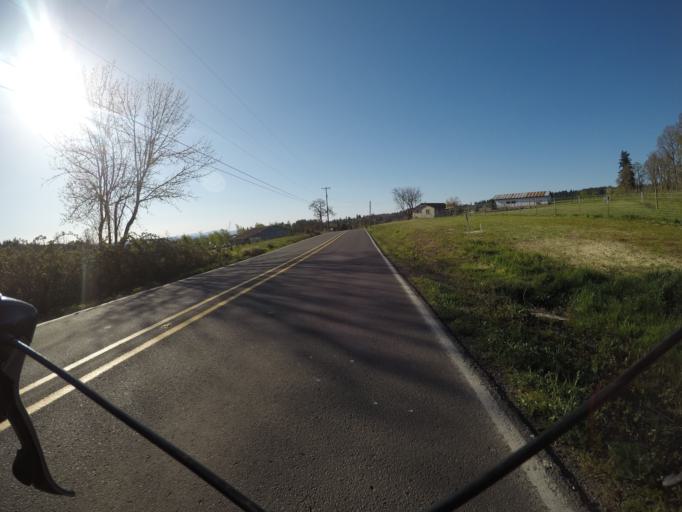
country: US
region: Oregon
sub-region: Washington County
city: Aloha
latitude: 45.4311
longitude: -122.8781
